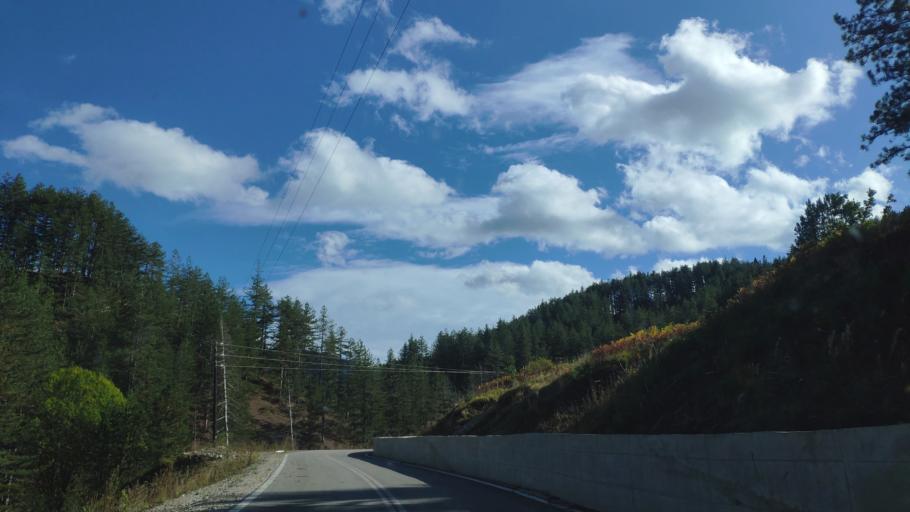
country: AL
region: Korce
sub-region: Rrethi i Devollit
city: Miras
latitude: 40.4068
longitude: 20.8772
